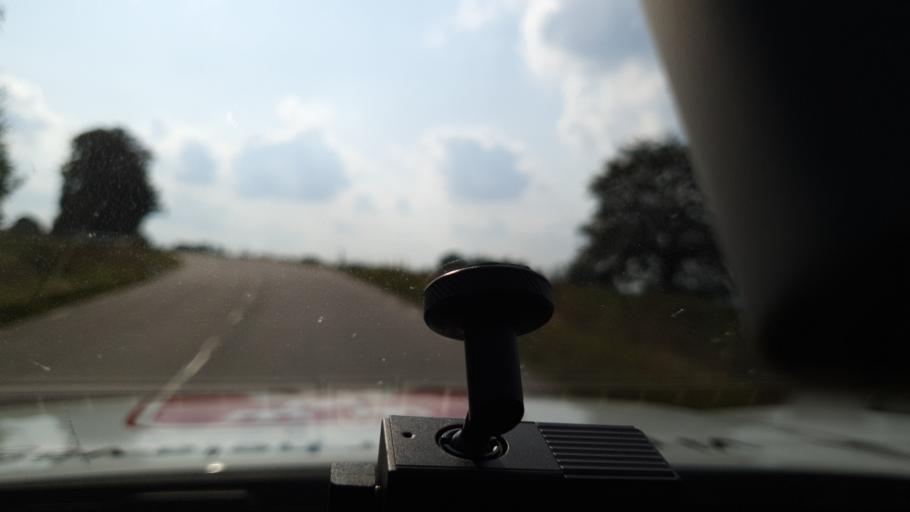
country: SE
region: Kalmar
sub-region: Vimmerby Kommun
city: Sodra Vi
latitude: 57.7167
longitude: 15.8369
